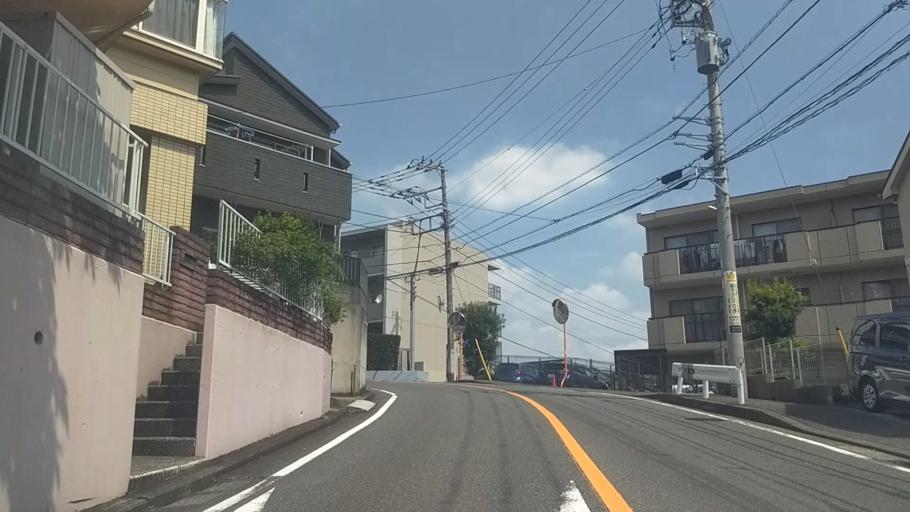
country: JP
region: Kanagawa
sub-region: Kawasaki-shi
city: Kawasaki
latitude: 35.5155
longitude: 139.6633
